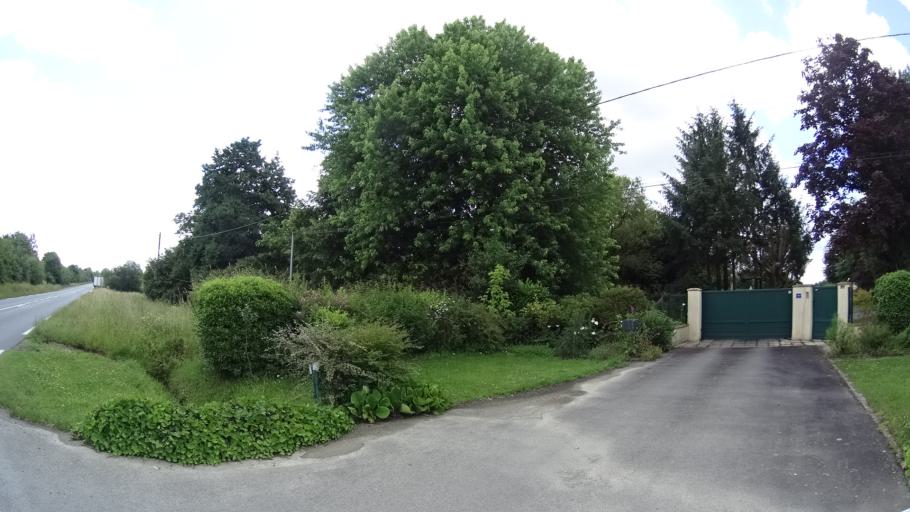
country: FR
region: Brittany
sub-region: Departement d'Ille-et-Vilaine
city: Le Rheu
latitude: 48.1164
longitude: -1.8186
